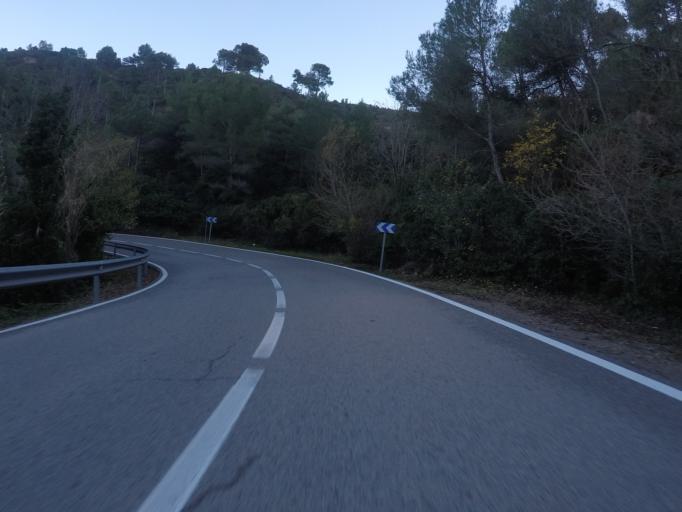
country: ES
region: Catalonia
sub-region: Provincia de Barcelona
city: Monistrol de Montserrat
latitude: 41.6140
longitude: 1.8316
